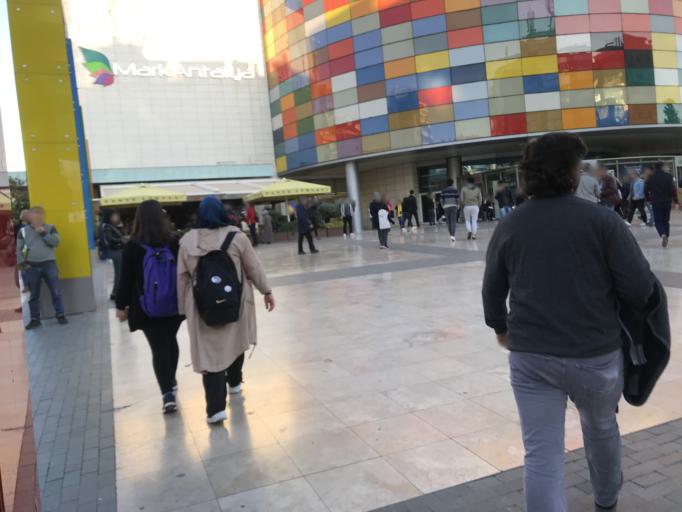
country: TR
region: Antalya
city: Antalya
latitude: 36.8929
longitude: 30.7028
